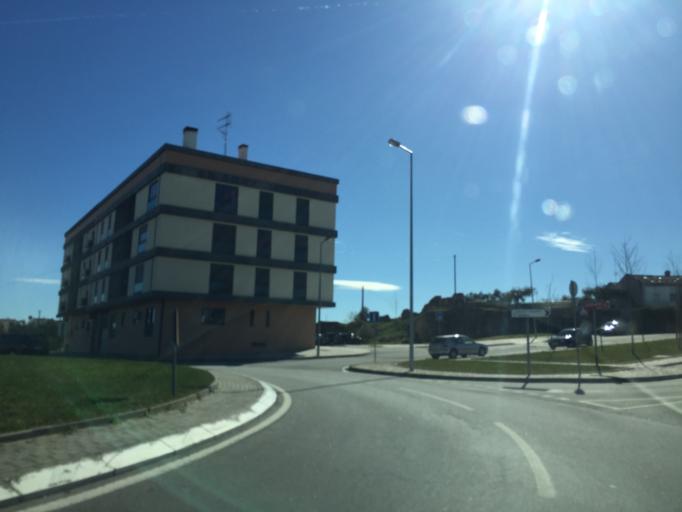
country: PT
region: Castelo Branco
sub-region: Castelo Branco
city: Castelo Branco
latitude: 39.8335
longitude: -7.4893
